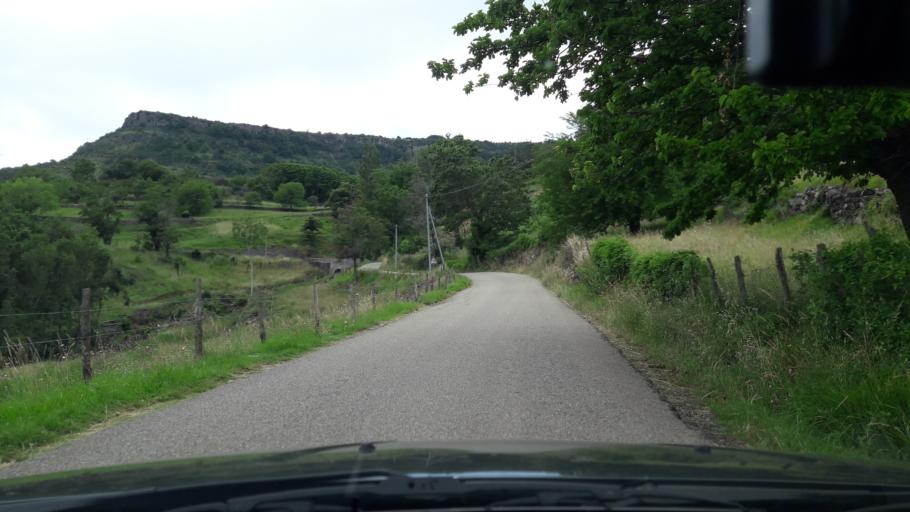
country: FR
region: Rhone-Alpes
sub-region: Departement de l'Ardeche
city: Alissas
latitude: 44.6851
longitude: 4.6313
